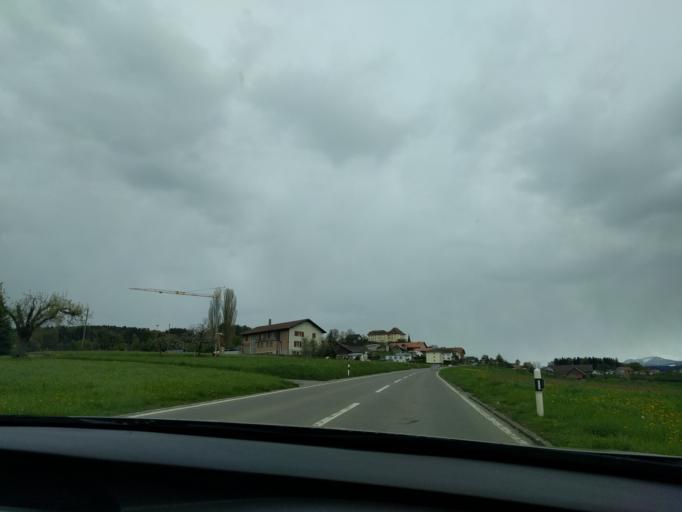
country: CH
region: Fribourg
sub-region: Sense District
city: Heitenried
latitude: 46.8305
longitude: 7.2913
